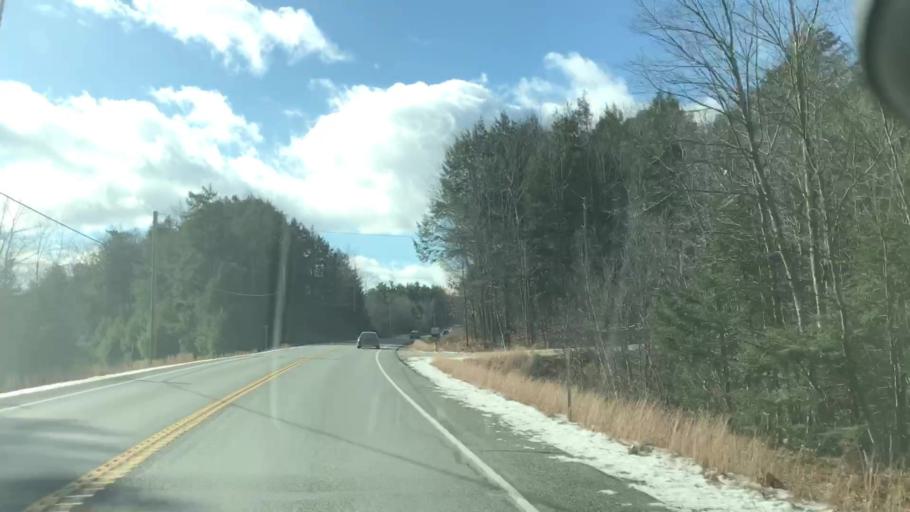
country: US
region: New Hampshire
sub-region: Carroll County
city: Ossipee
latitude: 43.6670
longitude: -71.1378
